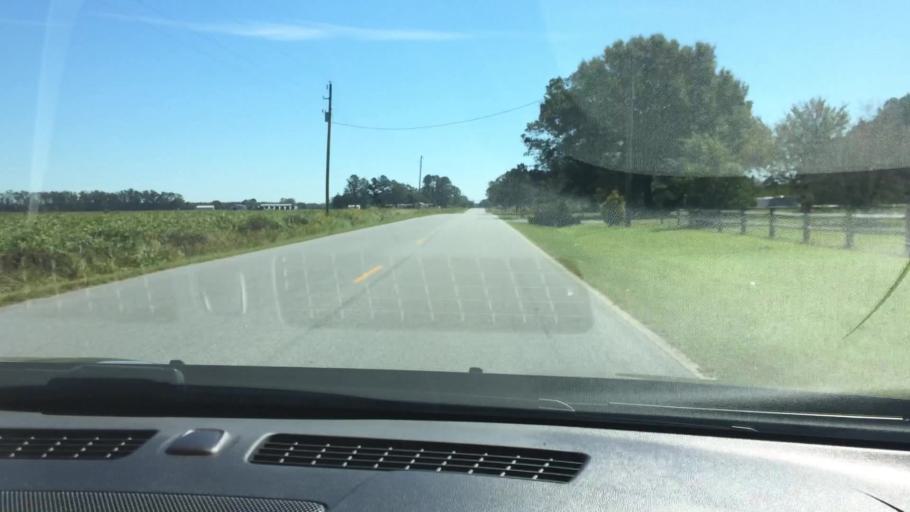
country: US
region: North Carolina
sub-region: Pitt County
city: Grifton
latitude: 35.3908
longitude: -77.3880
